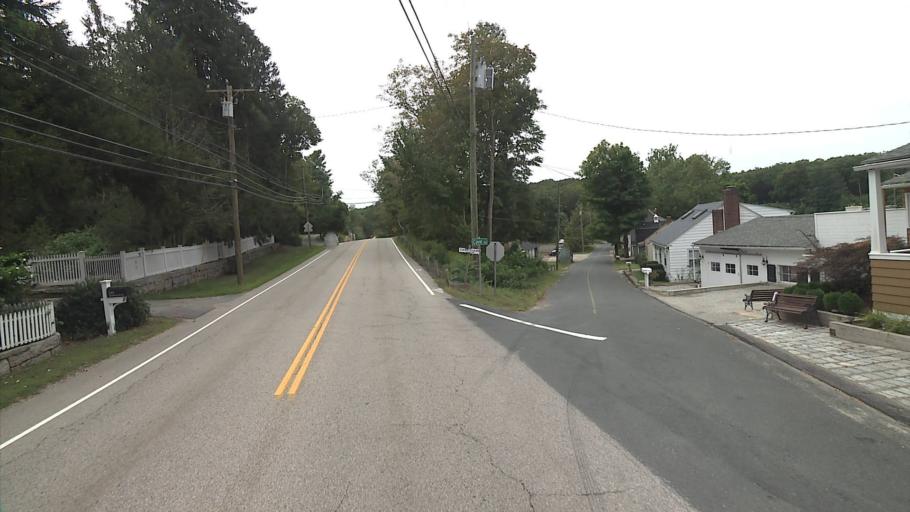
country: US
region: Connecticut
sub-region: Middlesex County
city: Essex Village
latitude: 41.3849
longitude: -72.3503
